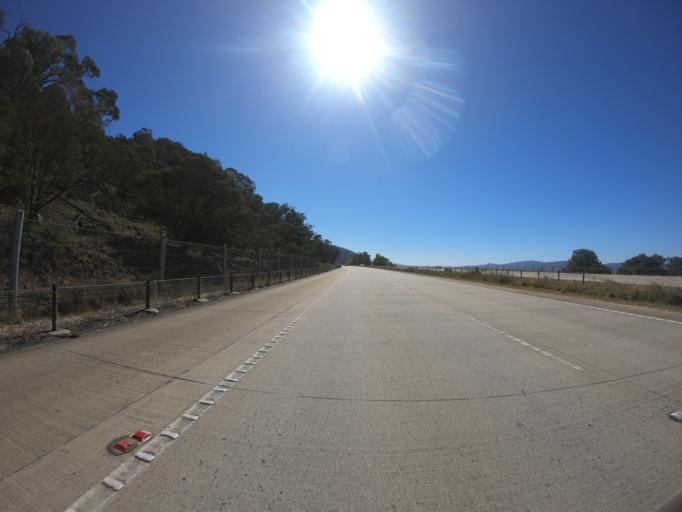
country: AU
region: New South Wales
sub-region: Yass Valley
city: Gundaroo
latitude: -35.0771
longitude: 149.3745
